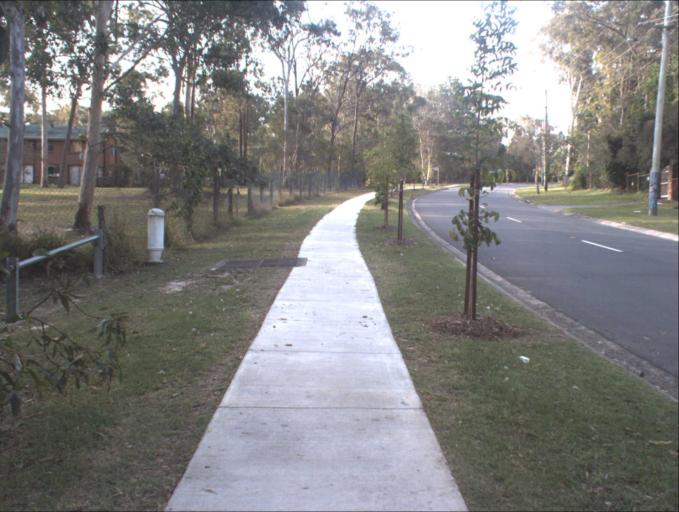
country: AU
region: Queensland
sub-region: Logan
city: Park Ridge South
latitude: -27.6726
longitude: 153.0134
